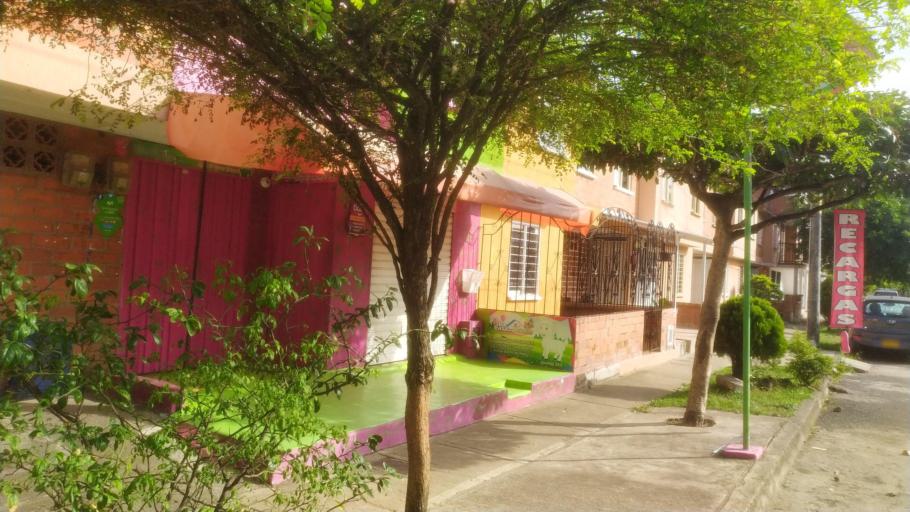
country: CO
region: Valle del Cauca
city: Jamundi
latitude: 3.2398
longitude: -76.5115
